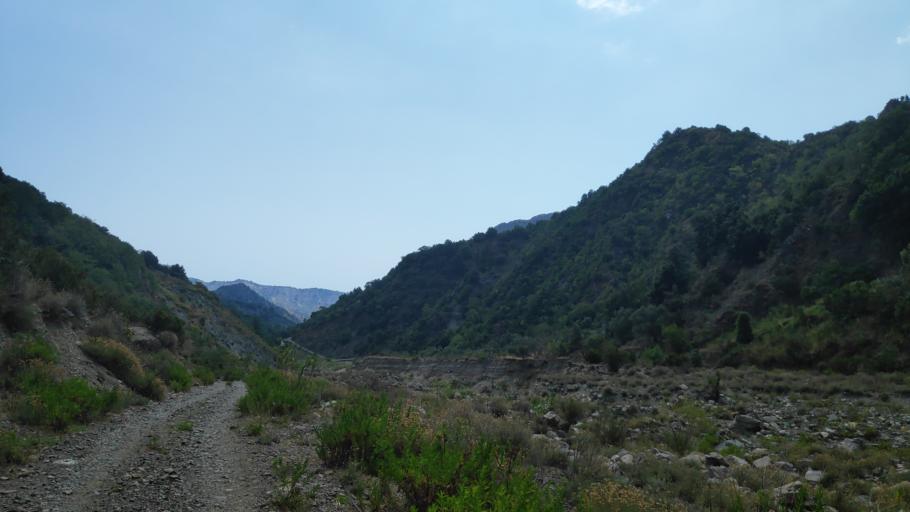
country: IT
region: Calabria
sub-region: Provincia di Reggio Calabria
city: Bivongi
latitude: 38.4945
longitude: 16.4471
